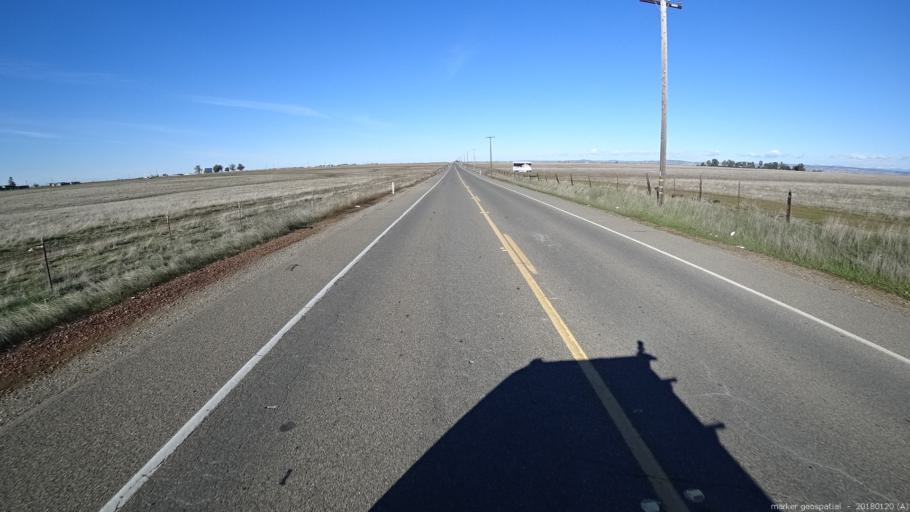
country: US
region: California
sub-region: Sacramento County
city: Rancho Murieta
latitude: 38.5438
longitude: -121.1872
